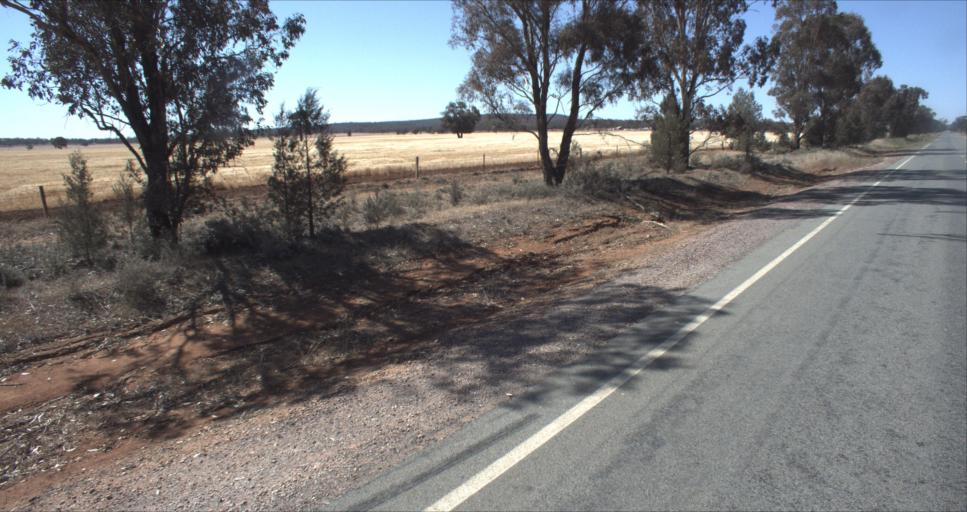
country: AU
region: New South Wales
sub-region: Leeton
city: Leeton
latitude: -34.4972
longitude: 146.4542
